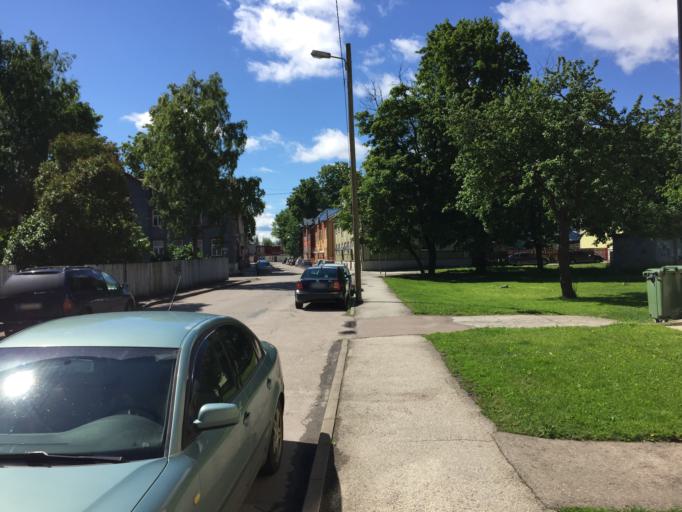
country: EE
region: Harju
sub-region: Tallinna linn
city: Tallinn
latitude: 59.4437
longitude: 24.7300
